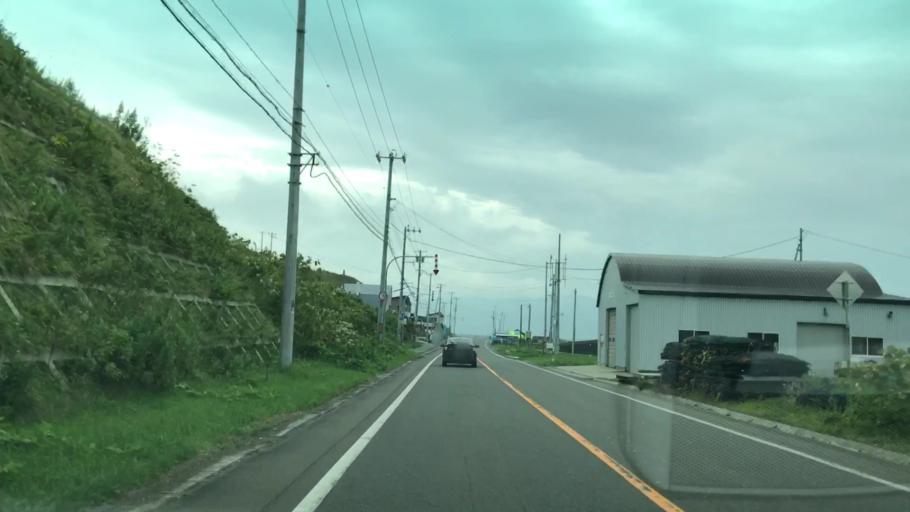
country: JP
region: Hokkaido
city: Iwanai
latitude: 42.8329
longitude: 140.3115
